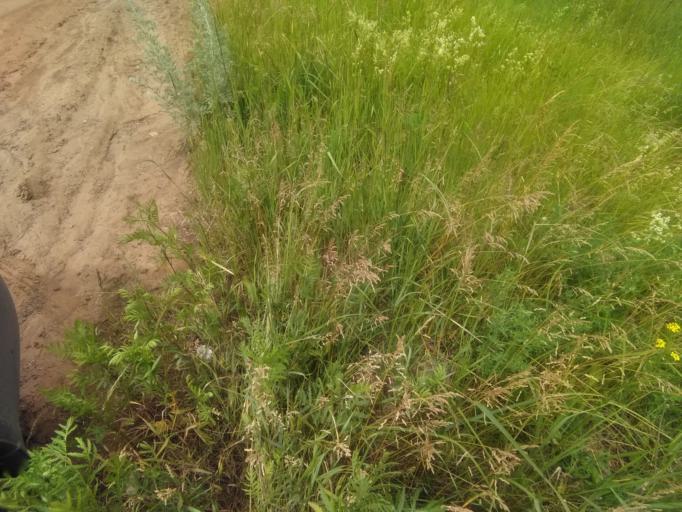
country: RU
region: Tatarstan
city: Yelabuga
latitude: 55.8026
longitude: 51.9470
